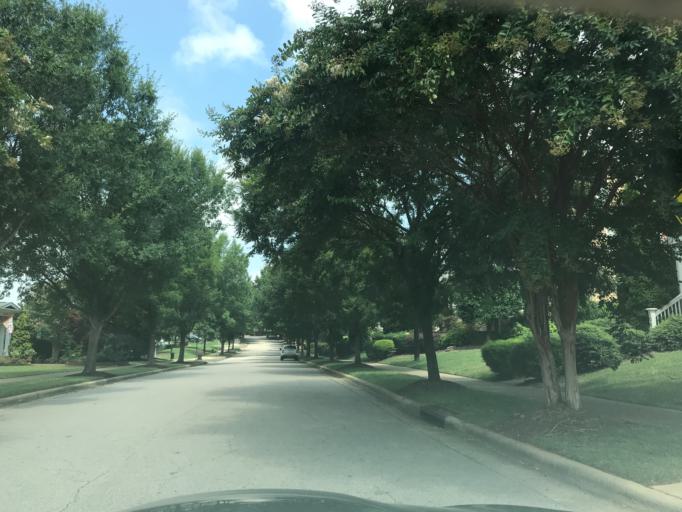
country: US
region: North Carolina
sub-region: Wake County
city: Wake Forest
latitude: 35.9244
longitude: -78.5641
